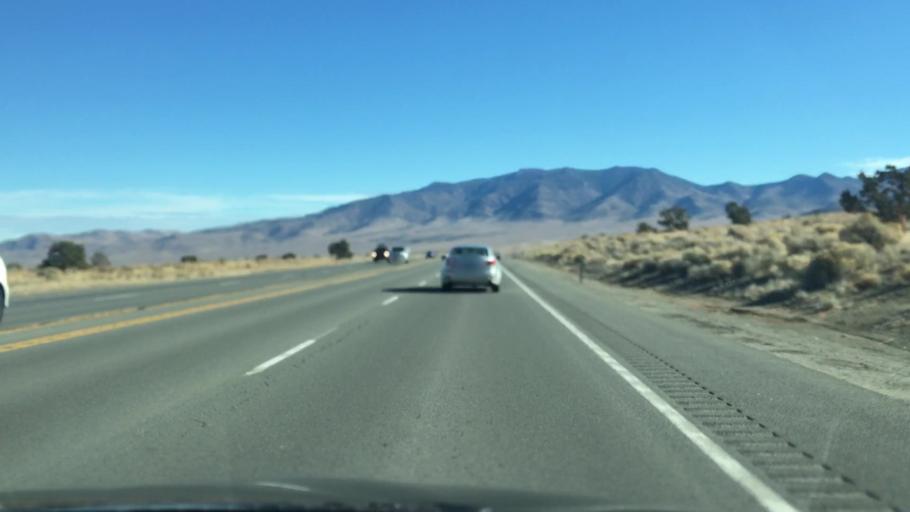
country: US
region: Nevada
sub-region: Lyon County
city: Dayton
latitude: 39.2233
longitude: -119.6282
